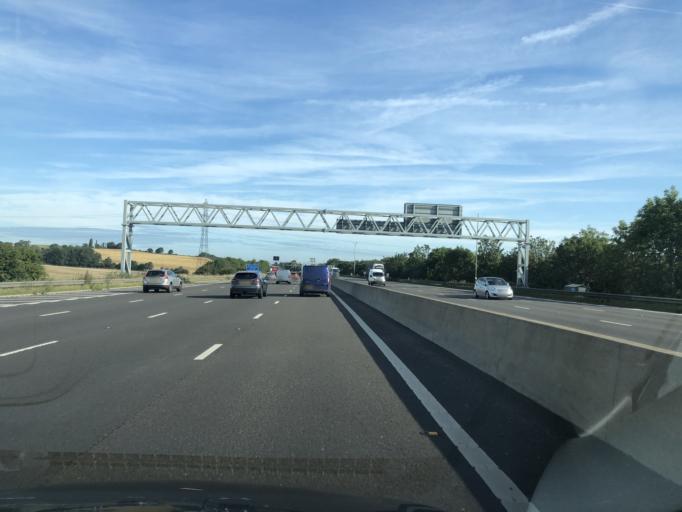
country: GB
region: England
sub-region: Derbyshire
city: Bolsover
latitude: 53.2043
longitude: -1.3218
